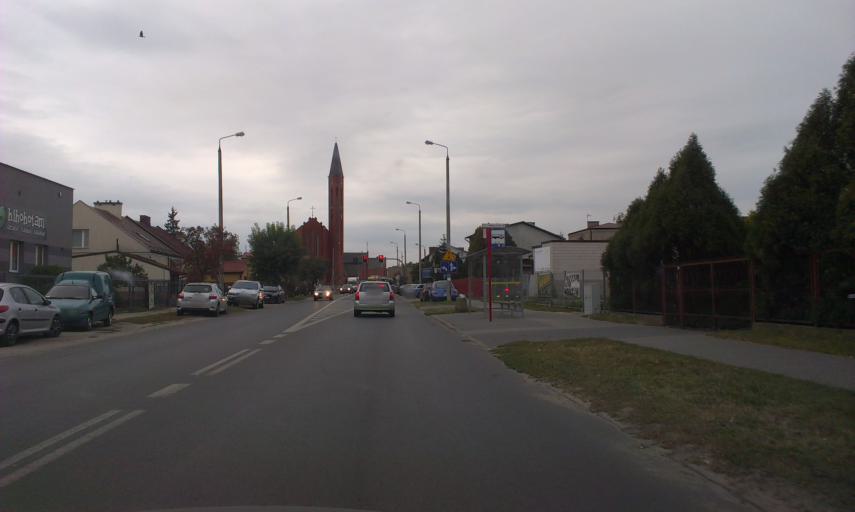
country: PL
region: Masovian Voivodeship
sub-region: Radom
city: Radom
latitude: 51.4105
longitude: 21.1358
